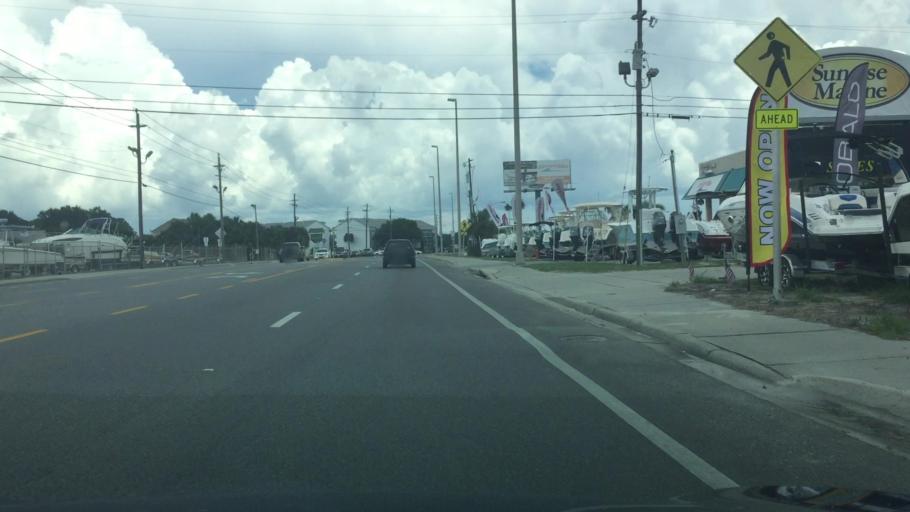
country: US
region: Florida
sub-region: Bay County
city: Lower Grand Lagoon
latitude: 30.1436
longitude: -85.7495
